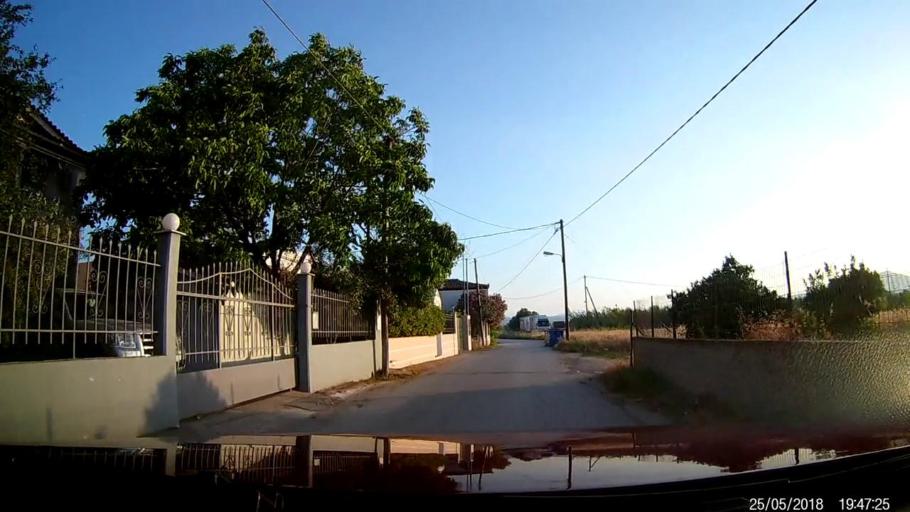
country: GR
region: Central Greece
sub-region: Nomos Evvoias
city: Ayios Nikolaos
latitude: 38.4224
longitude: 23.6383
